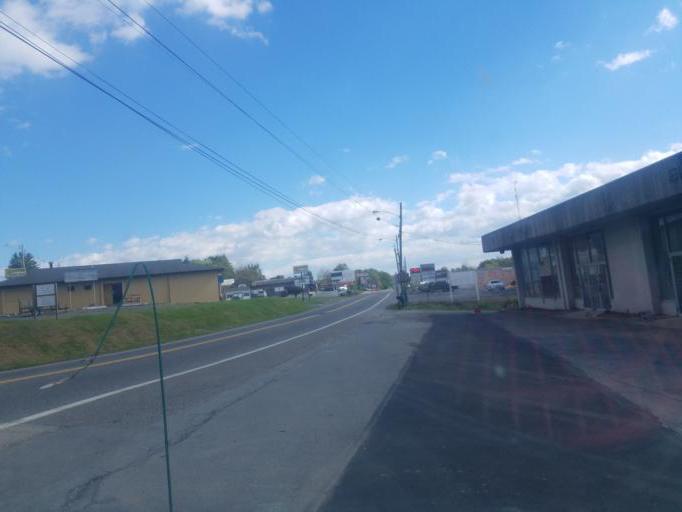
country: US
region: Pennsylvania
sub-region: Franklin County
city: Chambersburg
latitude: 39.9371
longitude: -77.6756
